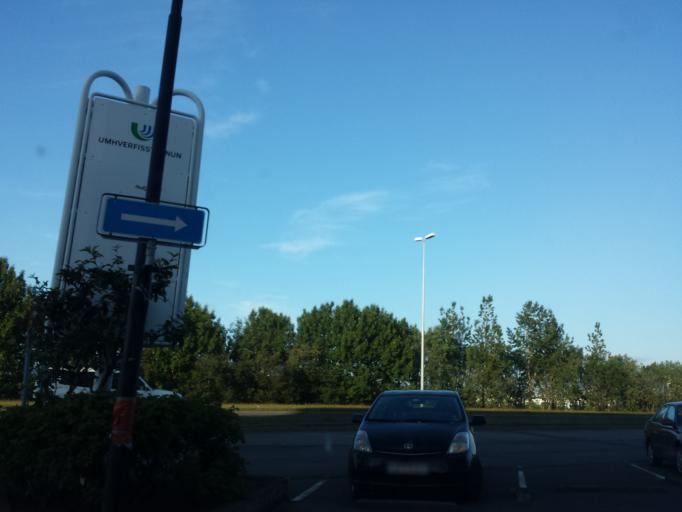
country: IS
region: Capital Region
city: Reykjavik
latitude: 64.1373
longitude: -21.8768
